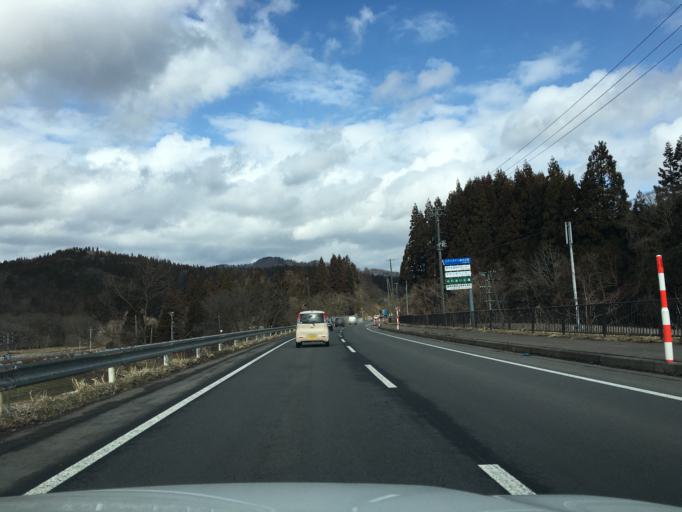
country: JP
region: Akita
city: Takanosu
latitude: 40.0262
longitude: 140.2739
